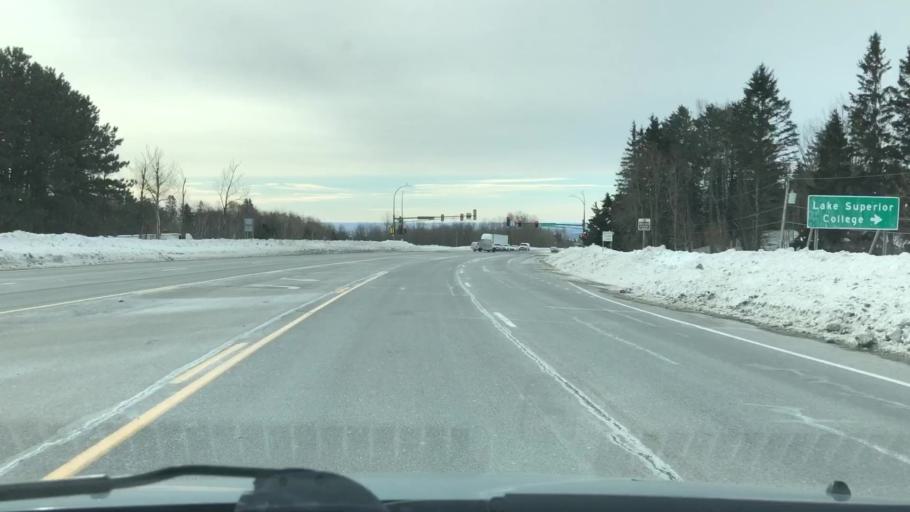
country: US
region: Minnesota
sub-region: Saint Louis County
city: Duluth
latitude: 46.7840
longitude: -92.1392
